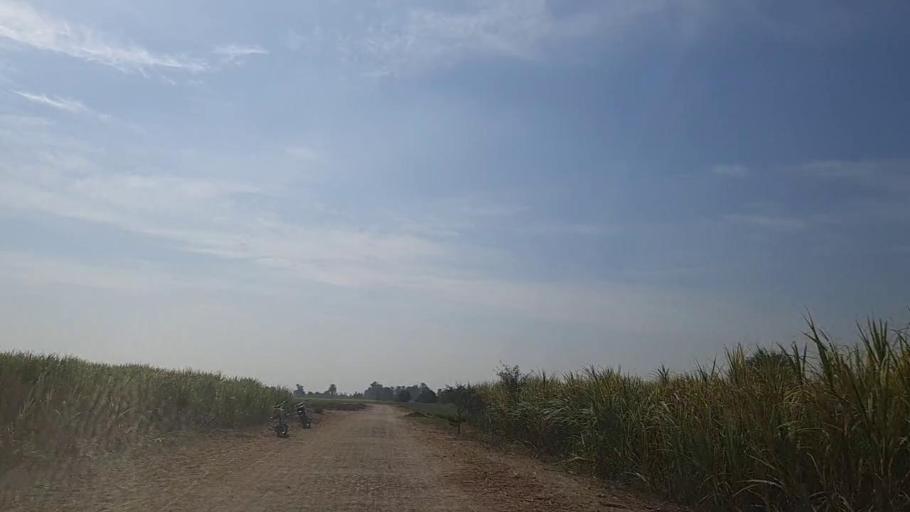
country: PK
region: Sindh
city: Mirpur Khas
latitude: 25.4737
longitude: 68.9640
